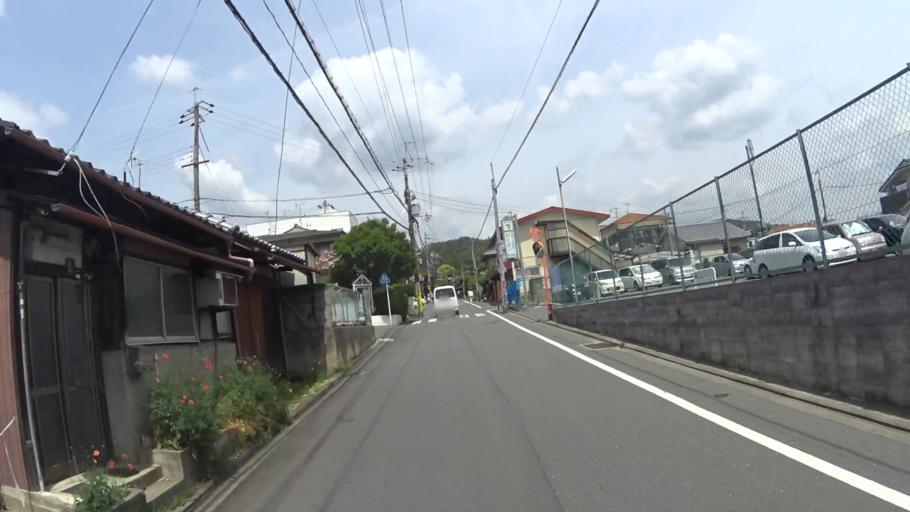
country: JP
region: Kyoto
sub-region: Kyoto-shi
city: Kamigyo-ku
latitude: 35.0524
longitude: 135.7333
